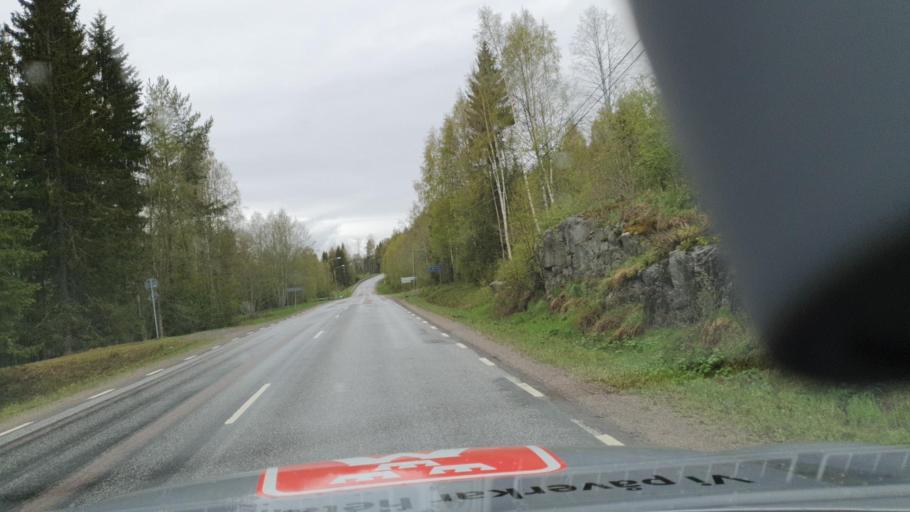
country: SE
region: Vaesternorrland
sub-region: OErnskoeldsviks Kommun
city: Bjasta
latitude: 63.3723
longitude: 18.4846
